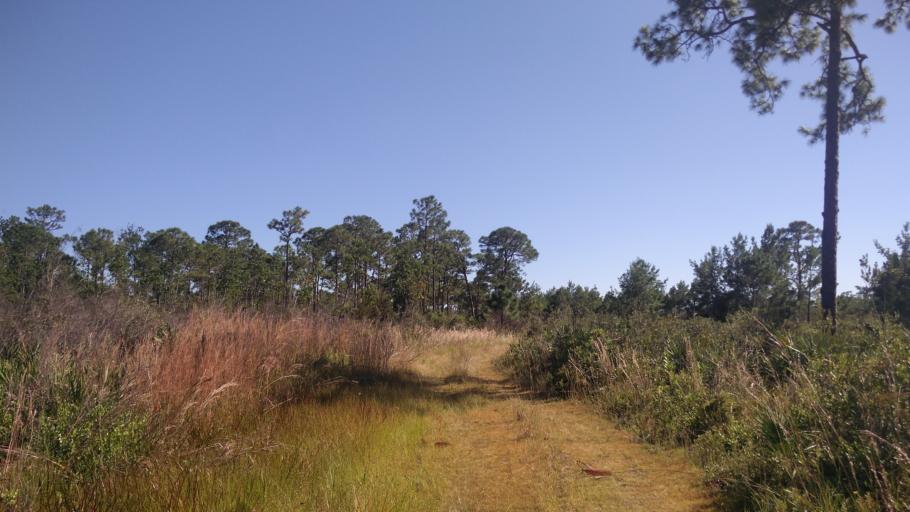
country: US
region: Florida
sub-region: Martin County
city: Hobe Sound
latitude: 27.0273
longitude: -80.1325
